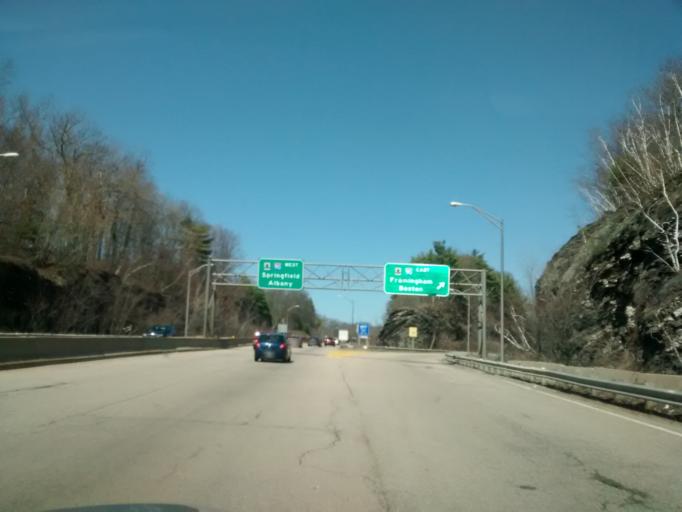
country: US
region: Massachusetts
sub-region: Worcester County
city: Auburn
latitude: 42.1903
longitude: -71.8538
